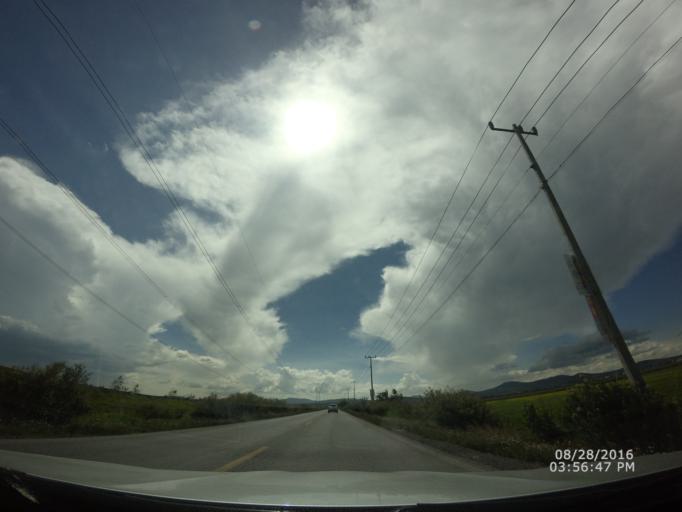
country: MX
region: Hidalgo
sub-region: Mineral de la Reforma
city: Los Tuzos
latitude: 20.0357
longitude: -98.7599
